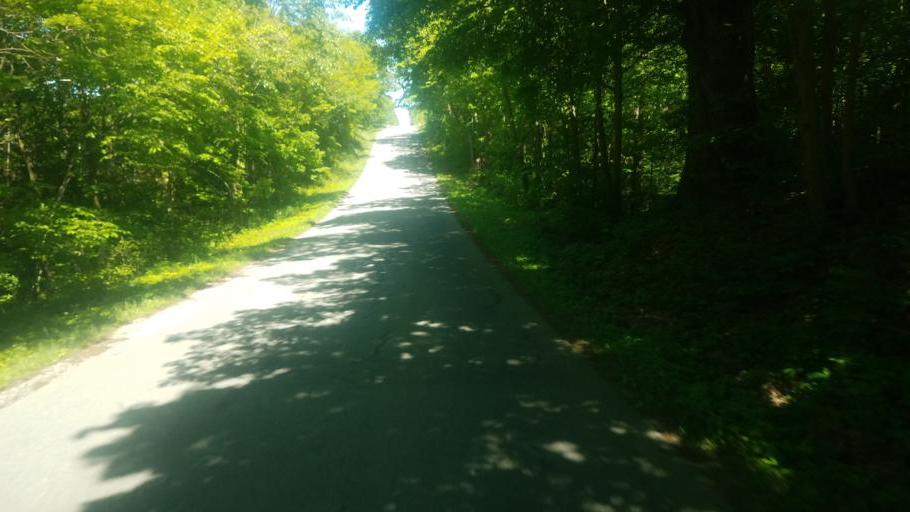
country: US
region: Ohio
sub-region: Logan County
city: Northwood
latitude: 40.4368
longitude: -83.7284
